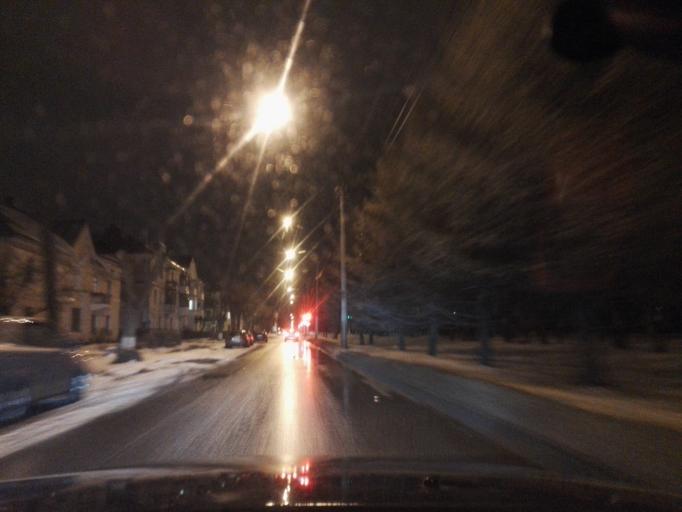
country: RU
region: Tula
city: Novomoskovsk
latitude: 54.0062
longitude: 38.2874
